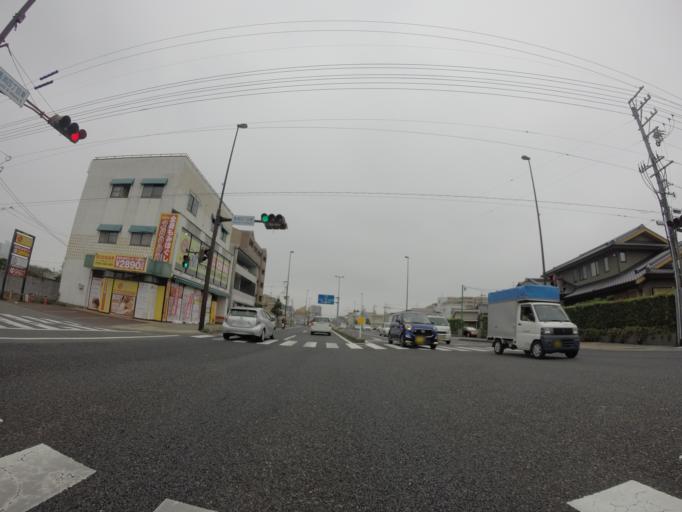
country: JP
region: Shizuoka
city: Shizuoka-shi
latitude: 34.9611
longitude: 138.3918
